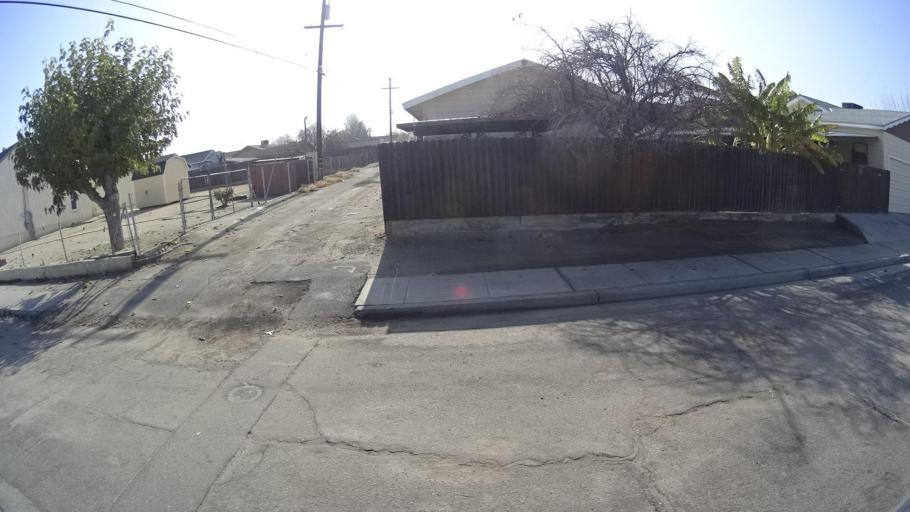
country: US
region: California
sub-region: Kern County
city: Ford City
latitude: 35.1576
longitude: -119.4596
